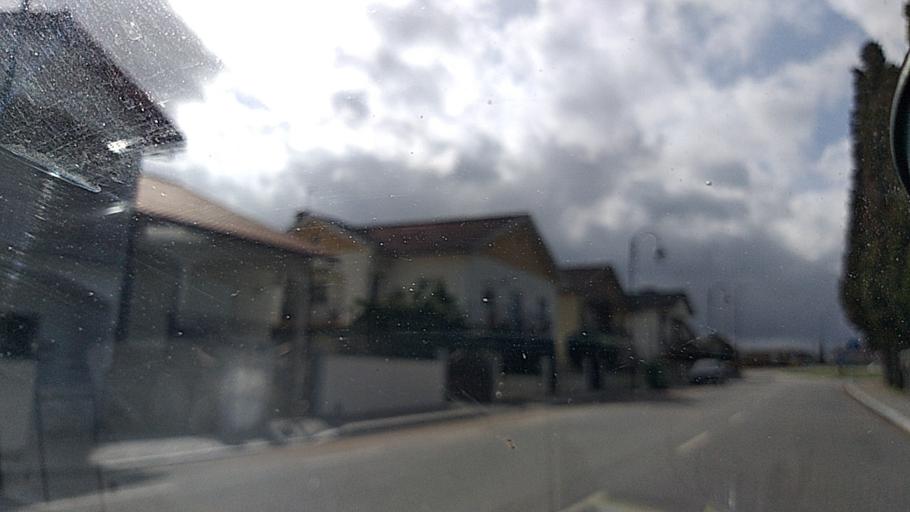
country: PT
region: Viseu
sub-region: Satao
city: Satao
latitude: 40.6718
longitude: -7.7016
